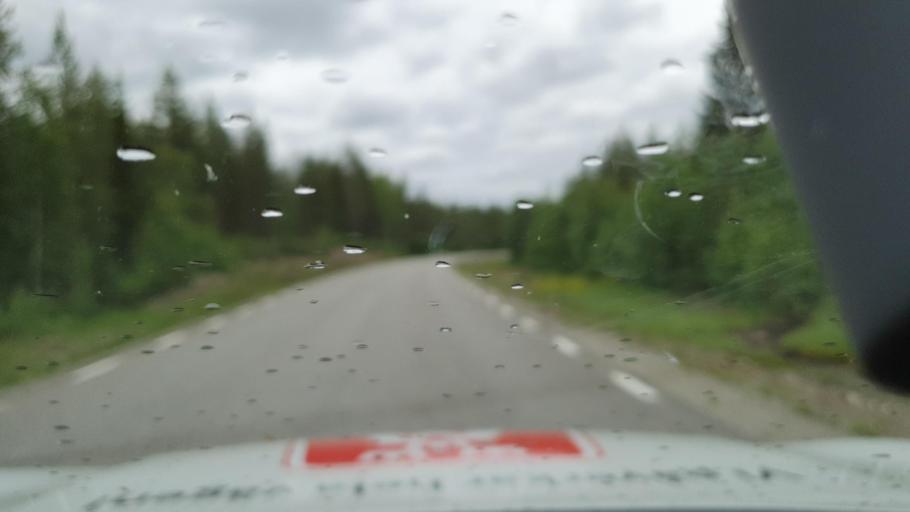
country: SE
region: Vaesterbotten
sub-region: Lycksele Kommun
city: Lycksele
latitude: 64.2322
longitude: 18.2386
